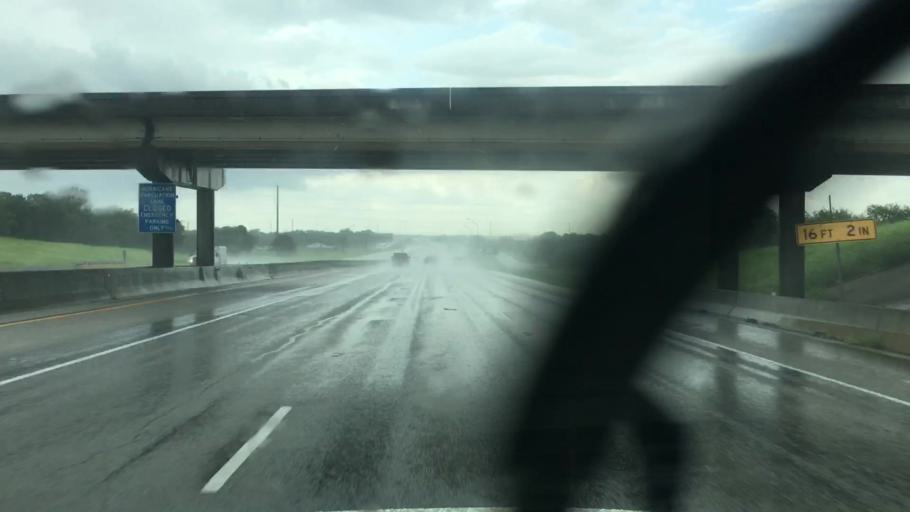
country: US
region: Texas
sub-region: Nueces County
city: Robstown
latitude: 27.8569
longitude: -97.6016
